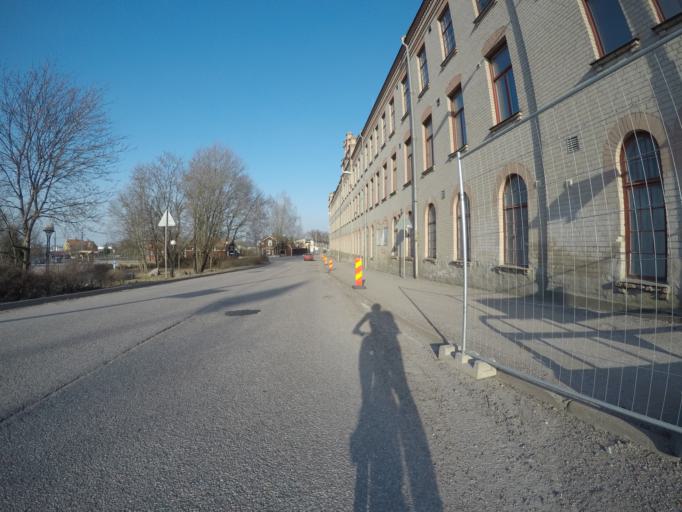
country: SE
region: Vaestmanland
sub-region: Kungsors Kommun
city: Kungsoer
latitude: 59.4268
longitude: 16.1014
